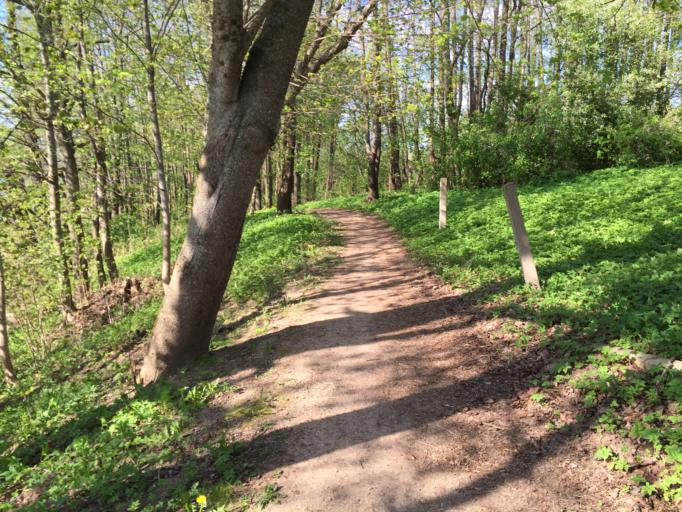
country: LV
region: Limbazu Rajons
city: Limbazi
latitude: 57.4937
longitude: 24.7057
